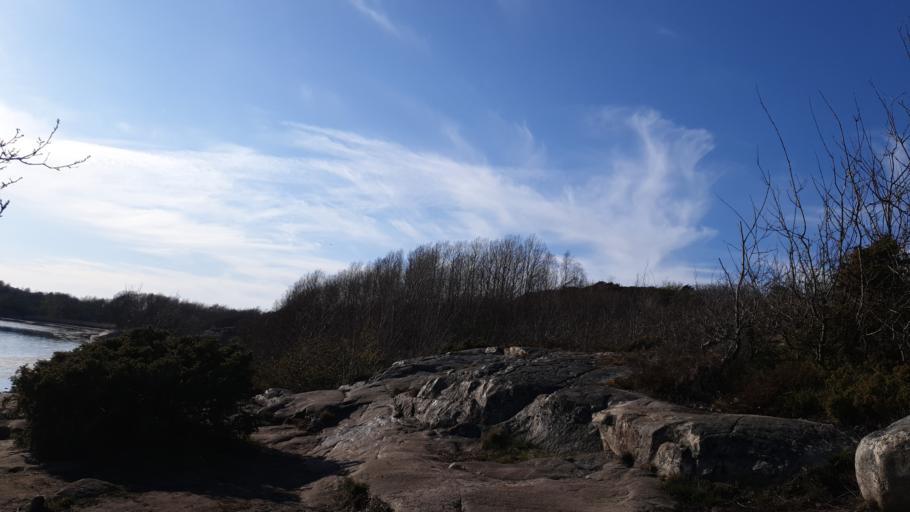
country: SE
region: Vaestra Goetaland
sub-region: Goteborg
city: Billdal
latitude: 57.5900
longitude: 11.9107
